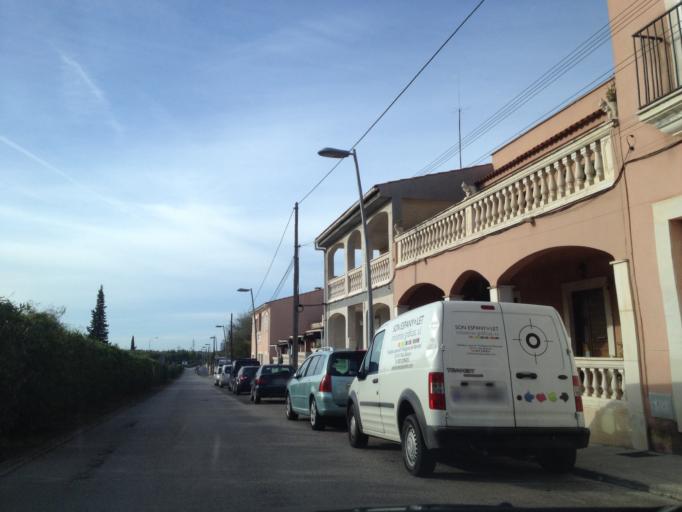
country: ES
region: Balearic Islands
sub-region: Illes Balears
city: Marratxi
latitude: 39.6237
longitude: 2.7273
